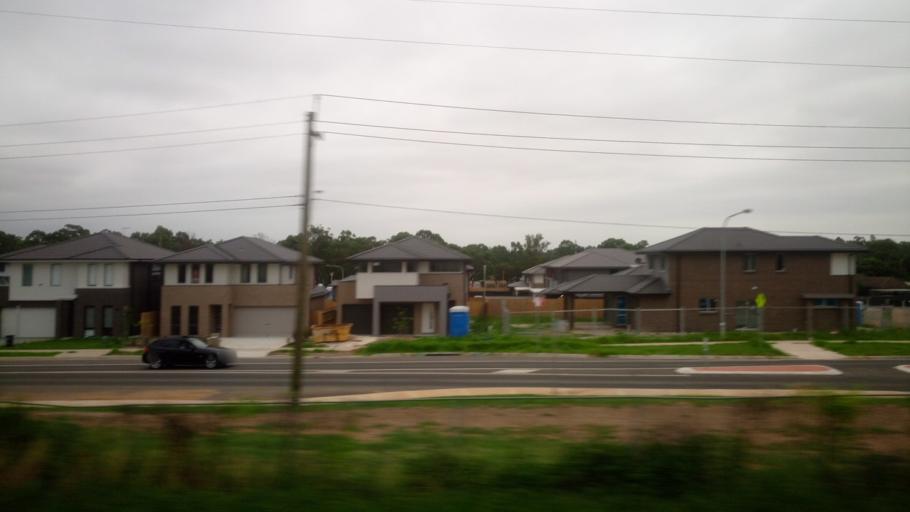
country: AU
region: New South Wales
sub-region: Penrith Municipality
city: Werrington County
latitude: -33.7581
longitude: 150.7396
